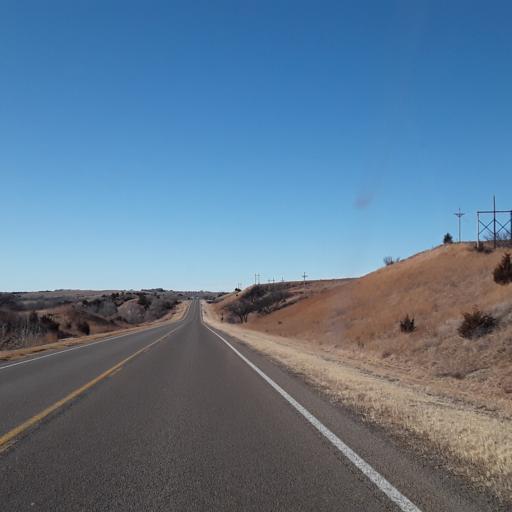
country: US
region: Nebraska
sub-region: Frontier County
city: Stockville
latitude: 40.6292
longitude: -100.5457
